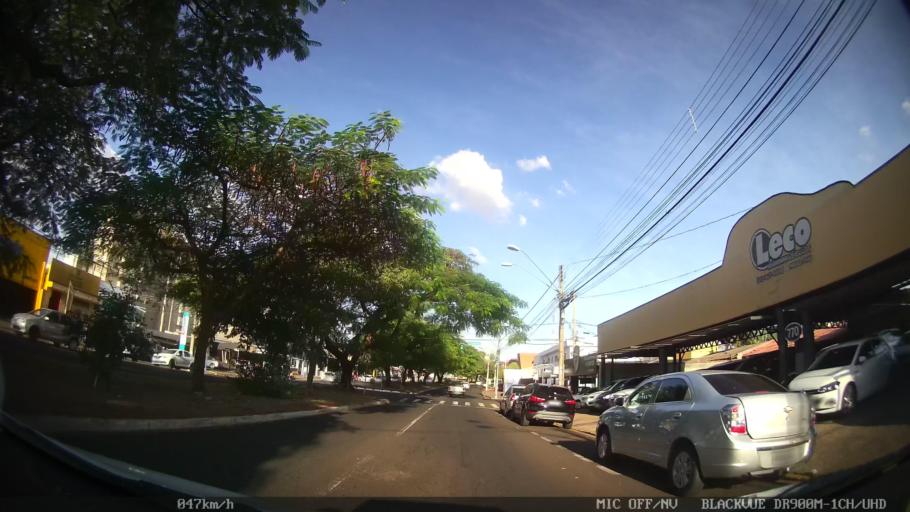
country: BR
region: Sao Paulo
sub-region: Ribeirao Preto
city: Ribeirao Preto
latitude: -21.1787
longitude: -47.7888
